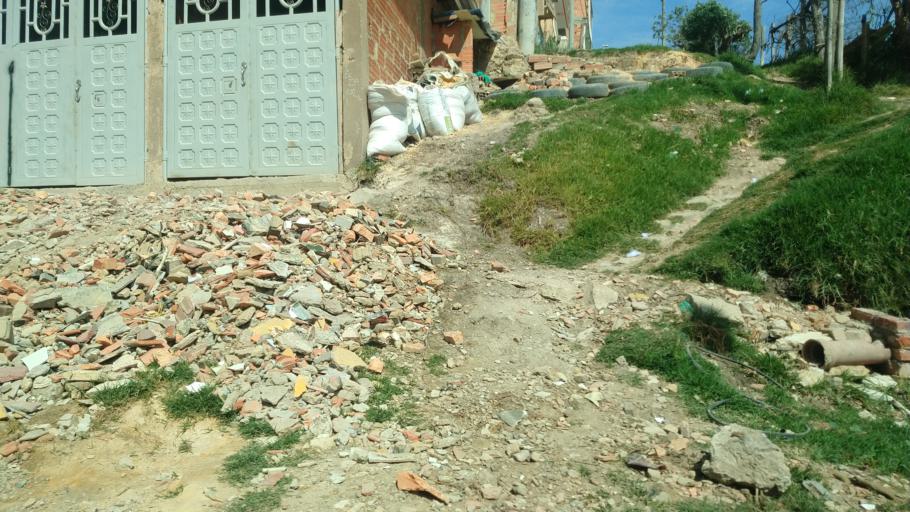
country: CO
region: Cundinamarca
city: Soacha
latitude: 4.5652
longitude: -74.1867
